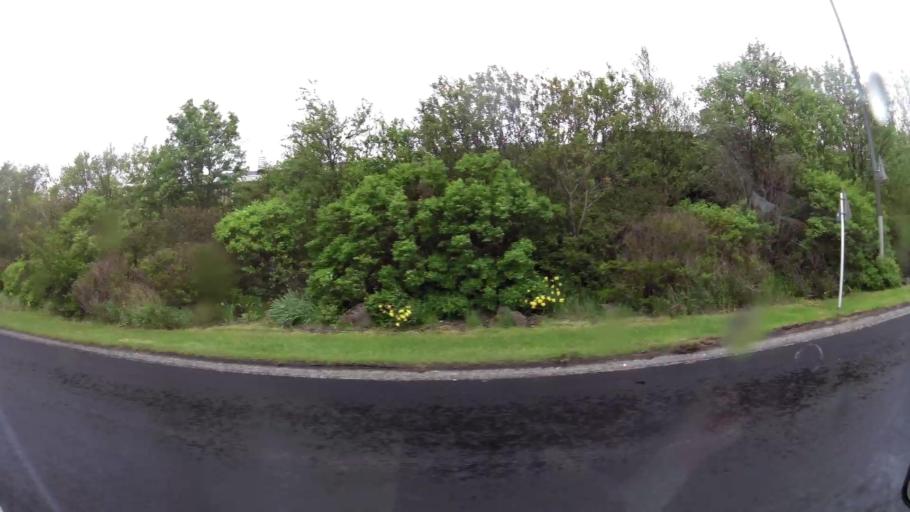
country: IS
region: Capital Region
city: Kopavogur
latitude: 64.0960
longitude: -21.9018
